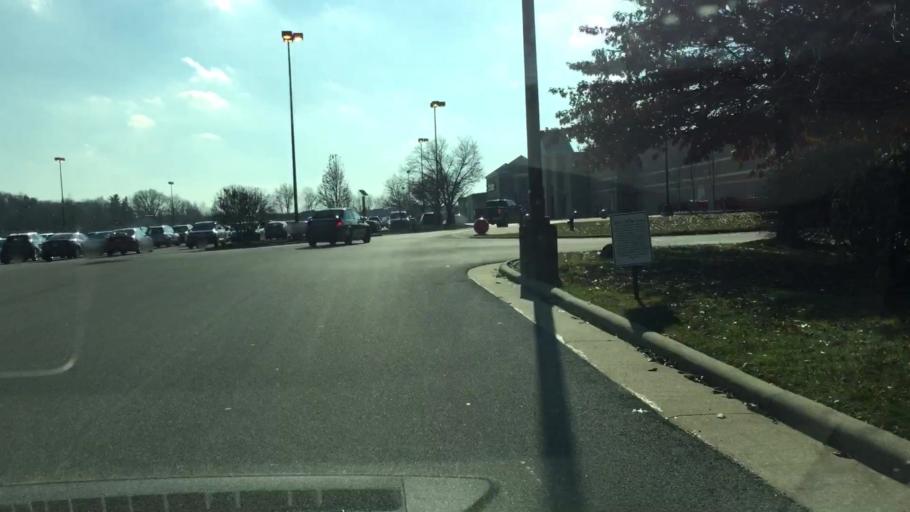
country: US
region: Ohio
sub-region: Summit County
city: Stow
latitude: 41.1569
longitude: -81.4102
